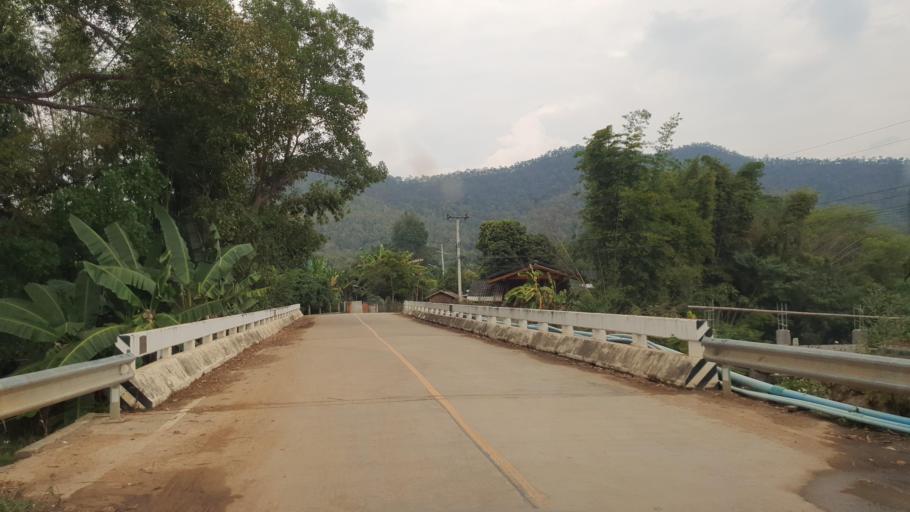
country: TH
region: Chiang Mai
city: Mae Wang
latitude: 18.6580
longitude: 98.6611
